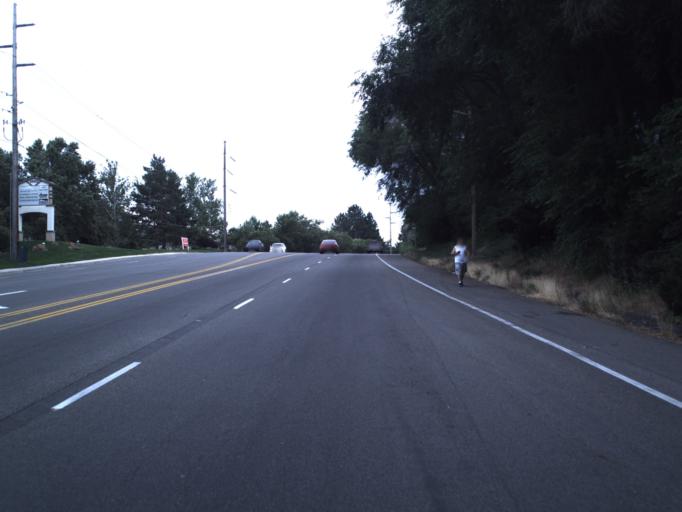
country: US
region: Utah
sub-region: Salt Lake County
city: Murray
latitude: 40.6645
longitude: -111.8648
